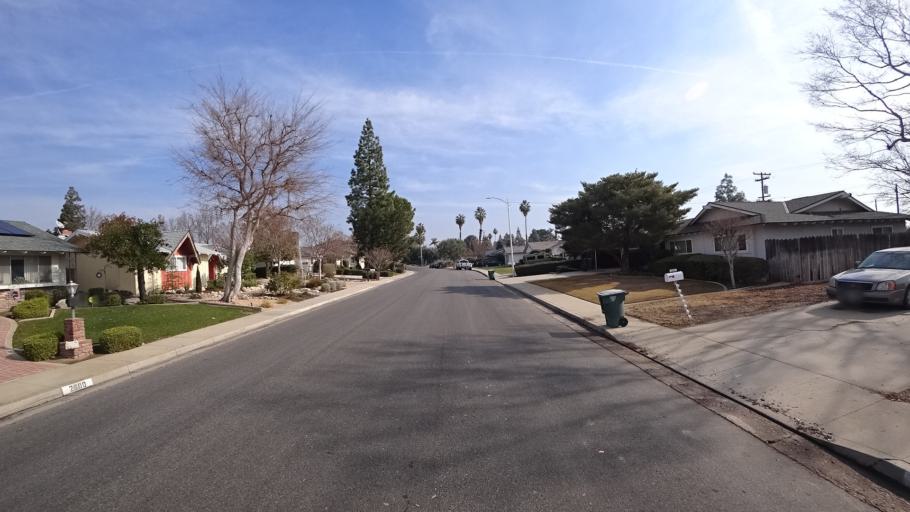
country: US
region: California
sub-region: Kern County
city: Oildale
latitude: 35.4128
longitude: -118.9646
